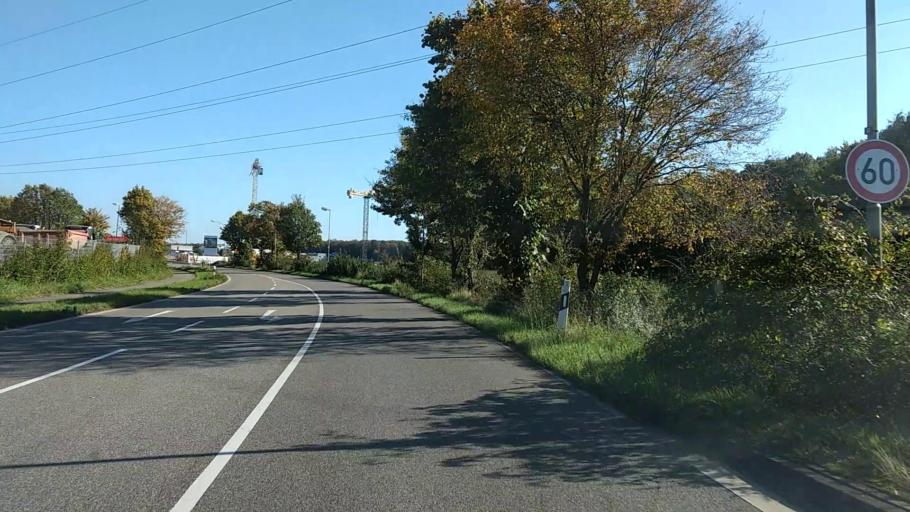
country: DE
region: North Rhine-Westphalia
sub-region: Regierungsbezirk Koln
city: Kerpen
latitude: 50.8933
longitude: 6.6642
